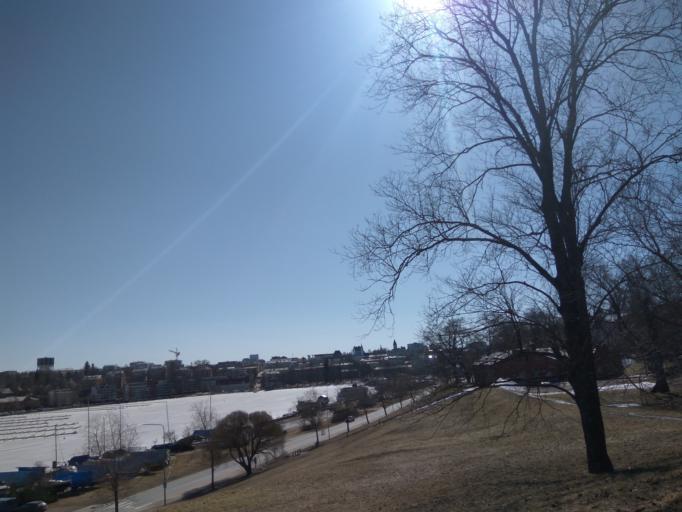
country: FI
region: South Karelia
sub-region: Lappeenranta
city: Lappeenranta
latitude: 61.0671
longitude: 28.1856
